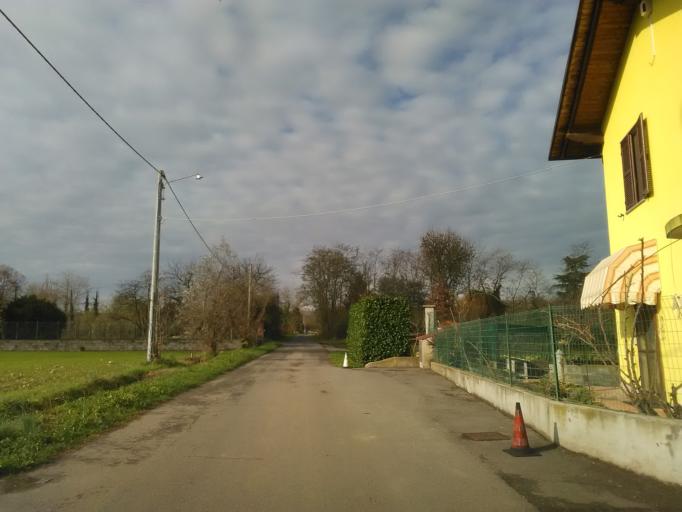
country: IT
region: Piedmont
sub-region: Provincia di Vercelli
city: Alice Castello
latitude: 45.3700
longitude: 8.0638
